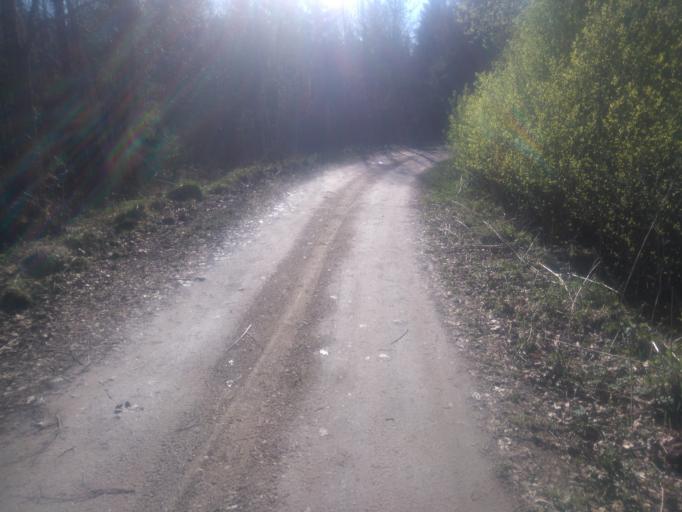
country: LV
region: Vecpiebalga
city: Vecpiebalga
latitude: 57.0068
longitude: 25.8469
